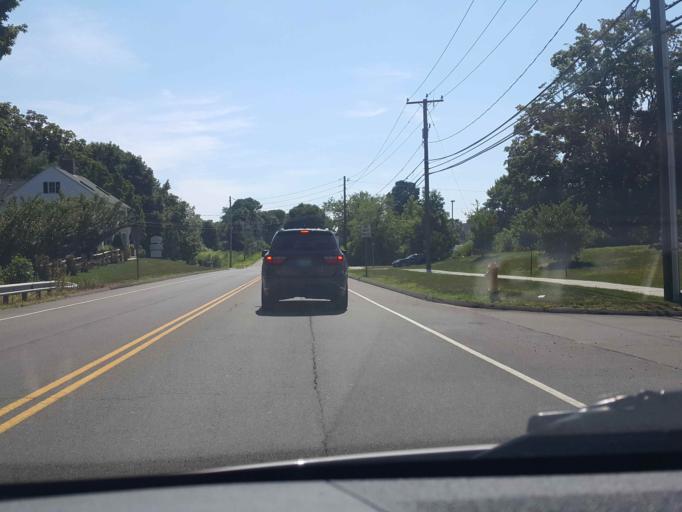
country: US
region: Connecticut
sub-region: New Haven County
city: North Branford
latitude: 41.3023
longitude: -72.7589
